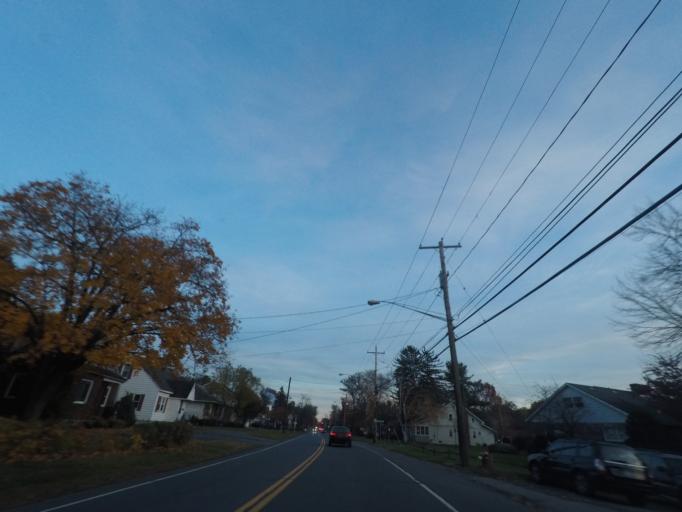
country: US
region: New York
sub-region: Schenectady County
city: Rotterdam
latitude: 42.7742
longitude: -73.9518
